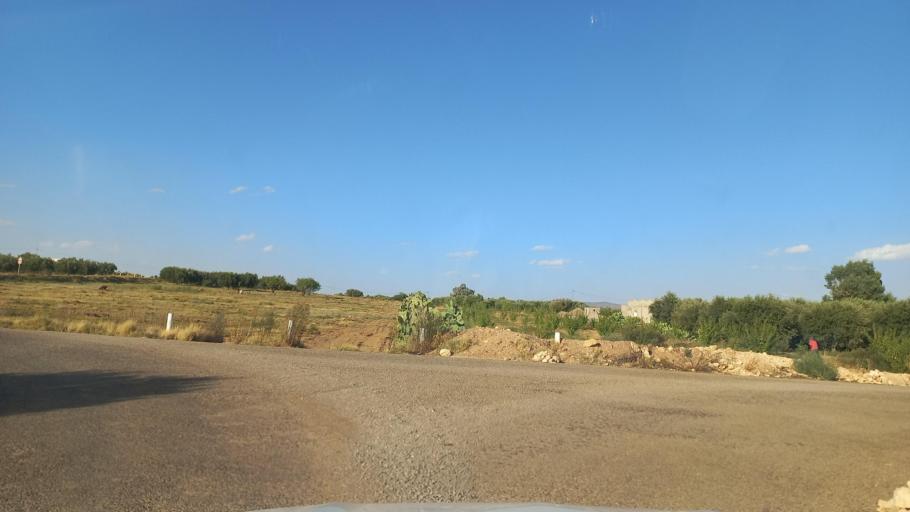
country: TN
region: Al Qasrayn
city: Kasserine
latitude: 35.2693
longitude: 9.0300
